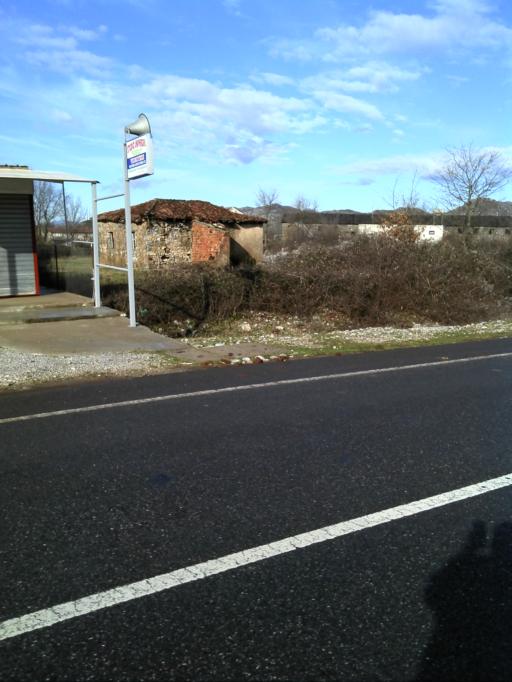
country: AL
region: Shkoder
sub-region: Rrethi i Malesia e Madhe
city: Koplik
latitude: 42.2865
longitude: 19.4404
